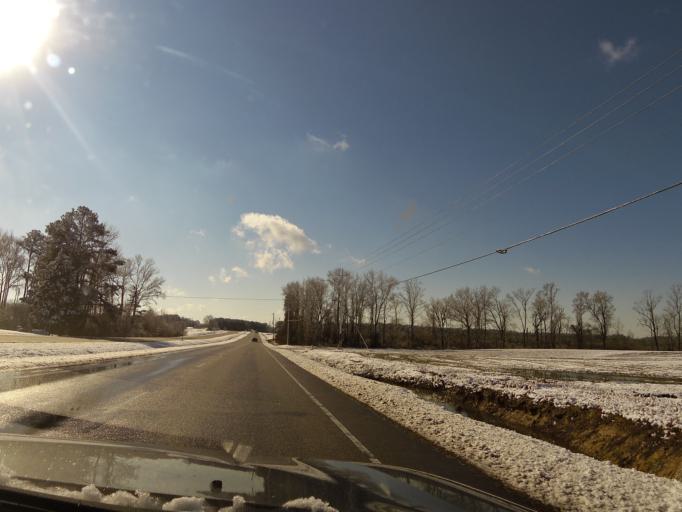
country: US
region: North Carolina
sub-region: Wilson County
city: Elm City
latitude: 35.7762
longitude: -77.8576
